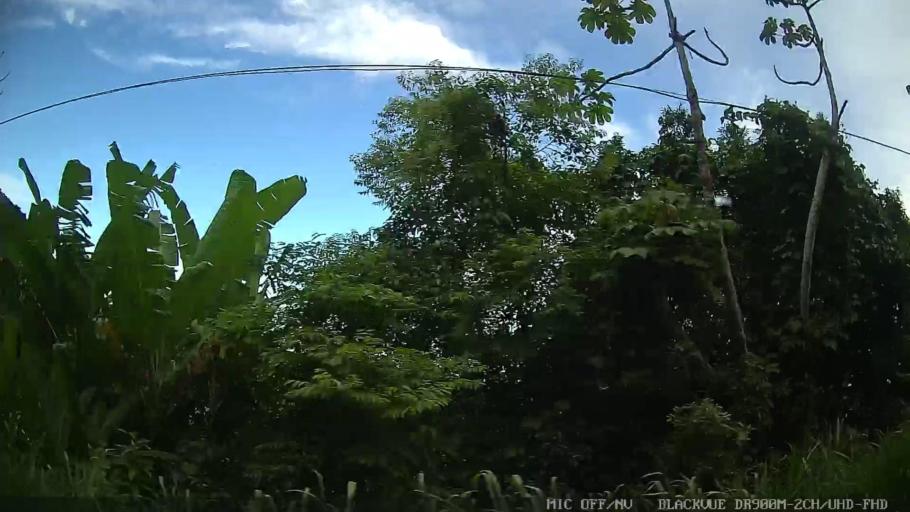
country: BR
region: Sao Paulo
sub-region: Iguape
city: Iguape
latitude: -24.7025
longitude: -47.5452
